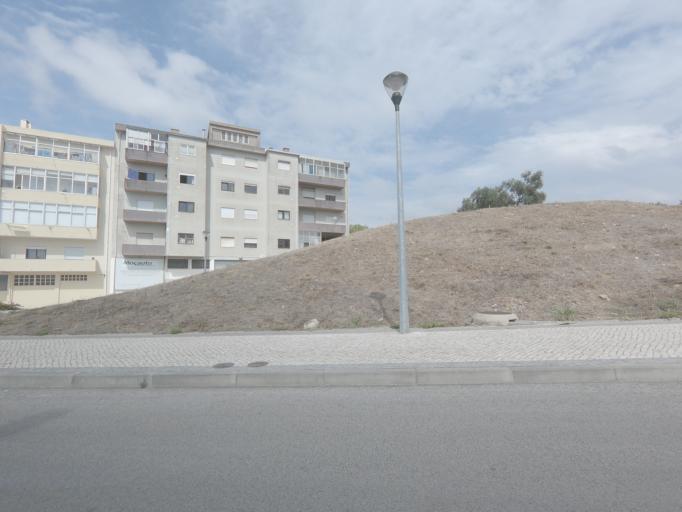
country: PT
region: Leiria
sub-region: Leiria
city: Leiria
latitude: 39.7451
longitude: -8.8170
